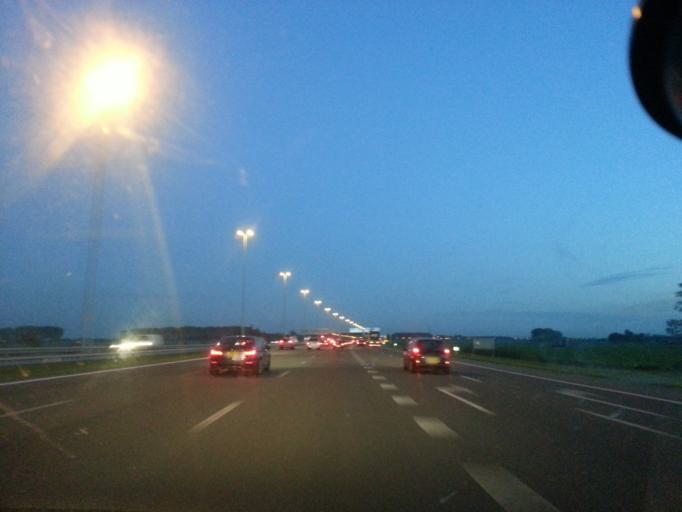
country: NL
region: Gelderland
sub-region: Gemeente Zaltbommel
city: Zaltbommel
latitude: 51.8724
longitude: 5.2148
